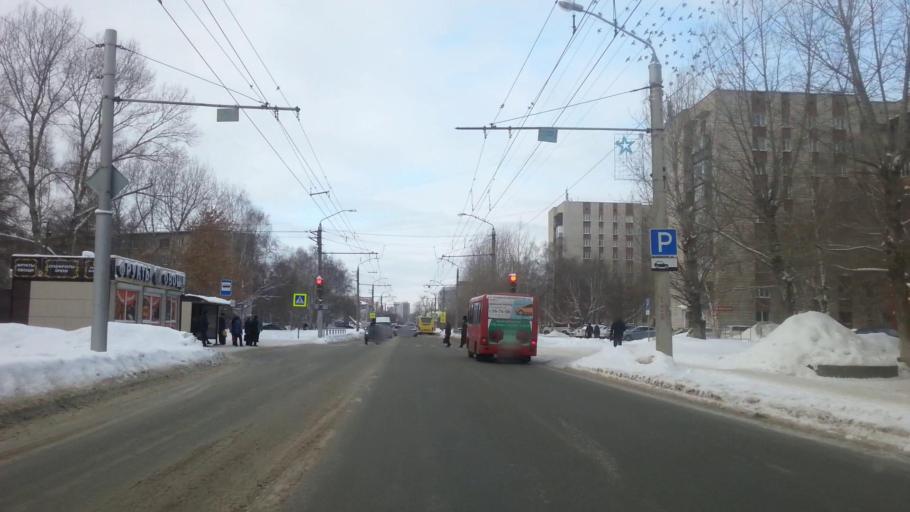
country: RU
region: Altai Krai
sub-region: Gorod Barnaulskiy
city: Barnaul
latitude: 53.3695
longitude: 83.6970
